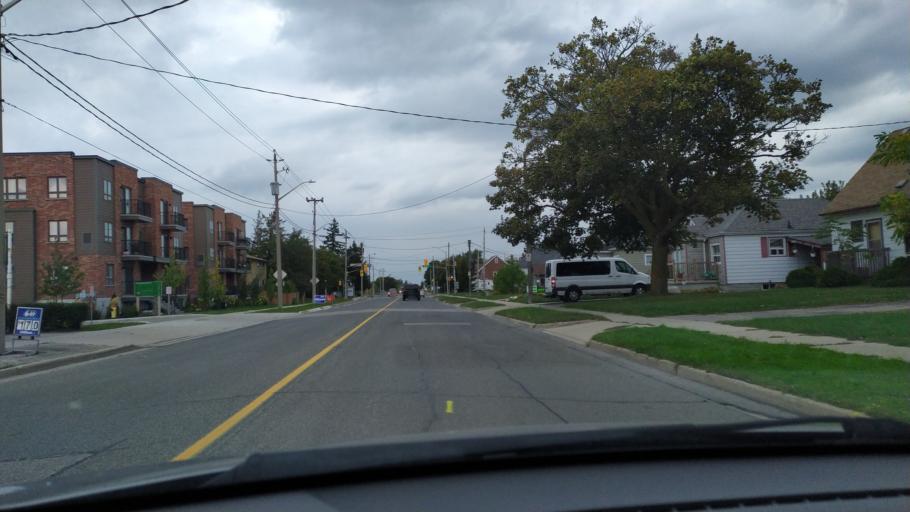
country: CA
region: Ontario
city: Waterloo
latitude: 43.4700
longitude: -80.4843
